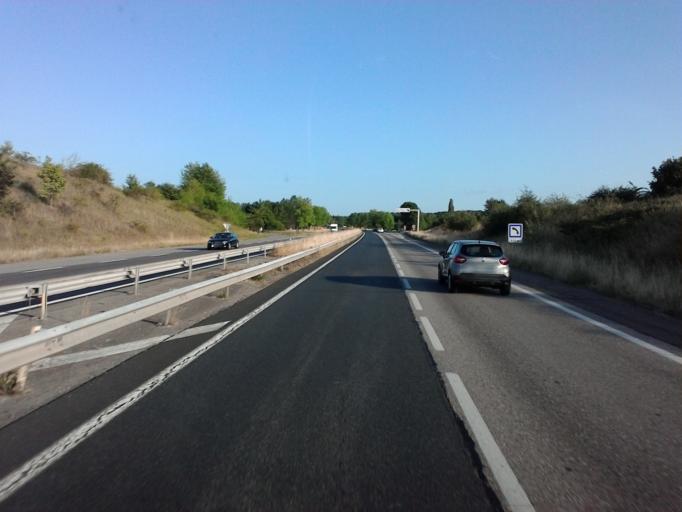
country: FR
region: Lorraine
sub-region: Departement des Vosges
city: Dogneville
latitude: 48.2151
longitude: 6.4553
